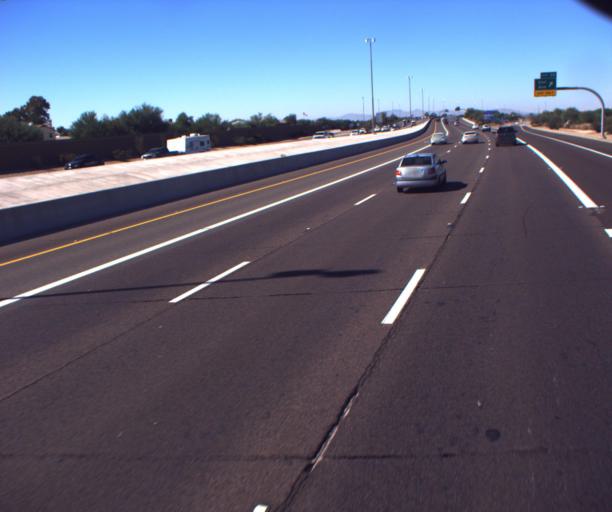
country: US
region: Arizona
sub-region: Maricopa County
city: Peoria
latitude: 33.6696
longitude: -112.1626
